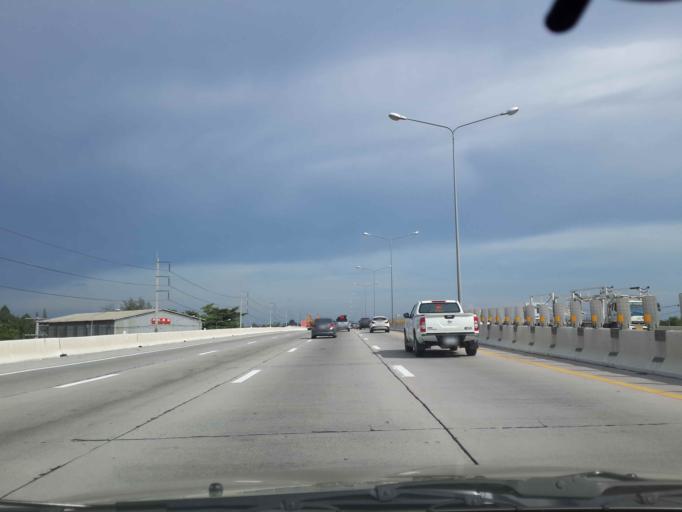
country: TH
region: Chon Buri
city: Si Racha
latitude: 13.2320
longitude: 101.0003
